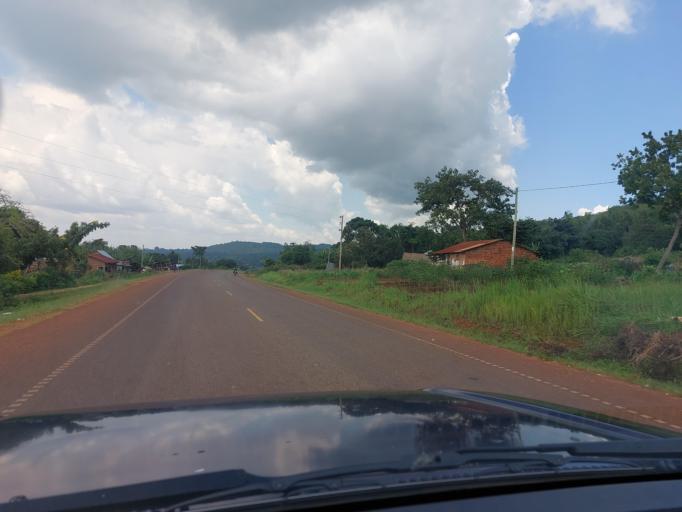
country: UG
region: Central Region
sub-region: Buikwe District
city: Njeru
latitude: 0.3338
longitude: 33.1209
